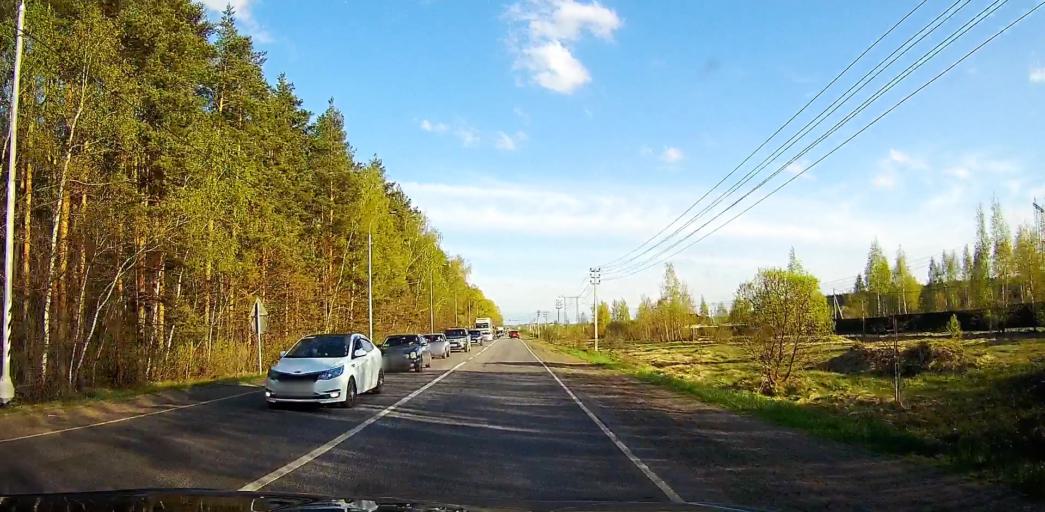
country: RU
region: Moskovskaya
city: Bronnitsy
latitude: 55.3797
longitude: 38.2091
